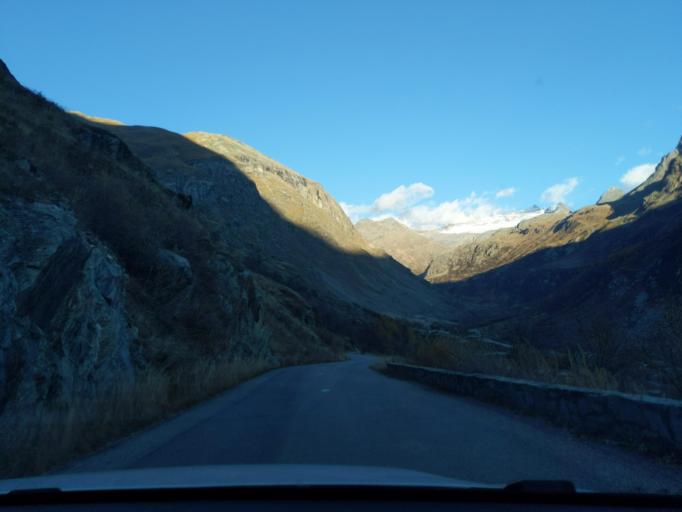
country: FR
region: Rhone-Alpes
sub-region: Departement de la Savoie
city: Val-d'Isere
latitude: 45.3728
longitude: 7.0397
